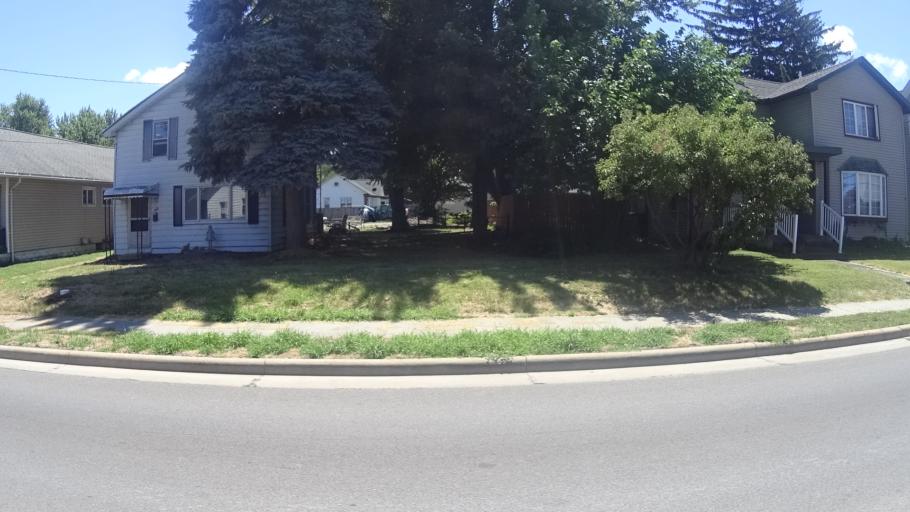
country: US
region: Ohio
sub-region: Erie County
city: Sandusky
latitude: 41.4531
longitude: -82.6972
